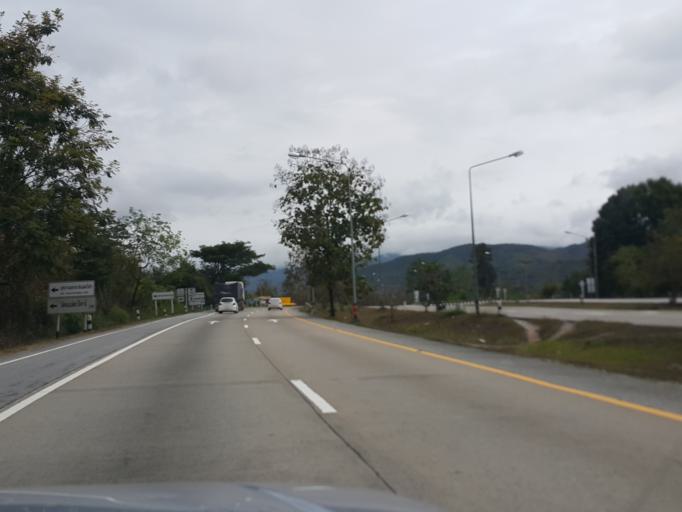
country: TH
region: Lamphun
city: Mae Tha
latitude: 18.4673
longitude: 99.1460
